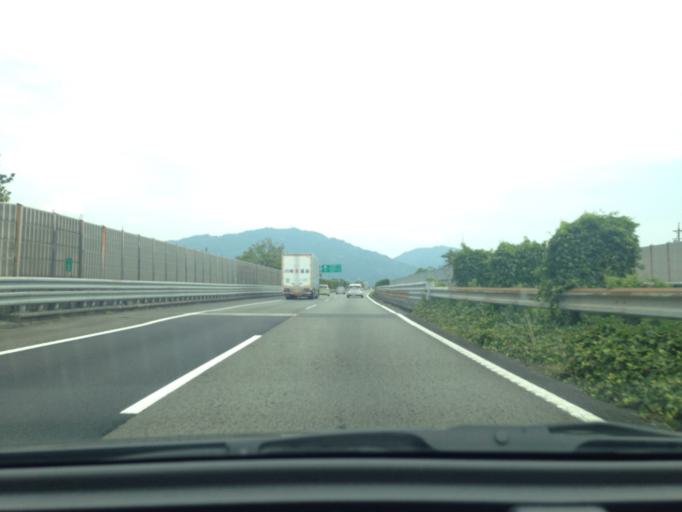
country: JP
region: Shizuoka
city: Fujieda
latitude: 34.8676
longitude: 138.2873
